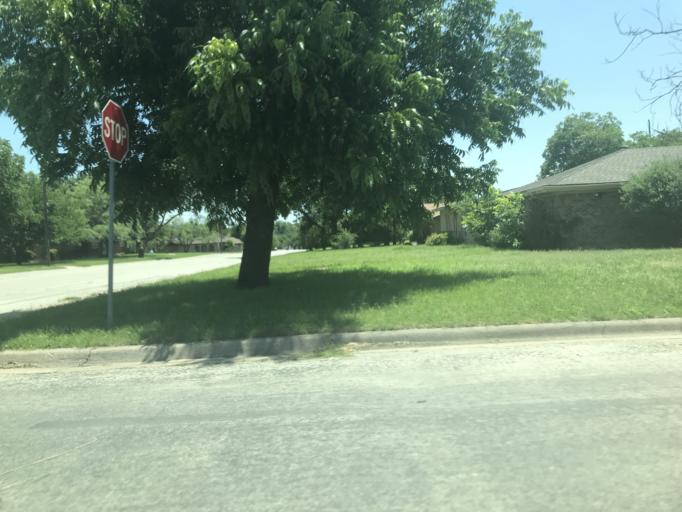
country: US
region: Texas
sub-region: Taylor County
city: Abilene
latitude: 32.4609
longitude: -99.7098
